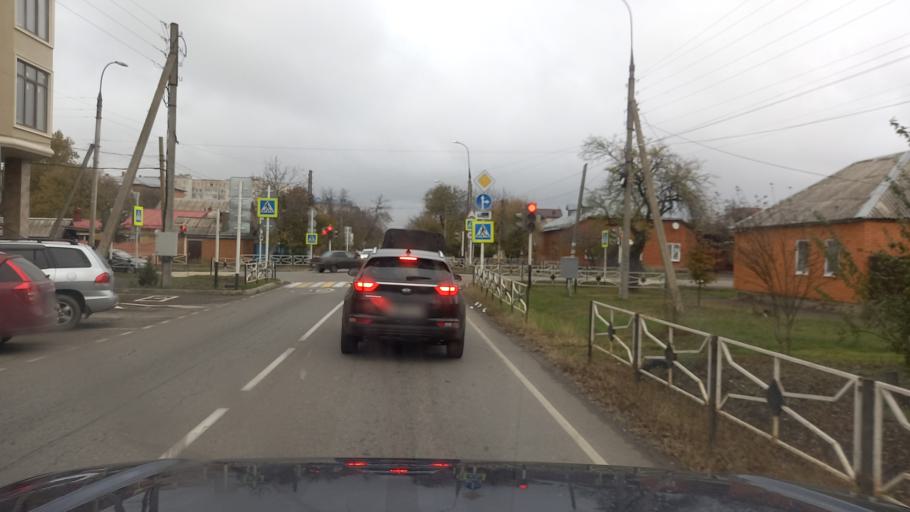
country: RU
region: Adygeya
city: Maykop
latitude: 44.6074
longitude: 40.0718
